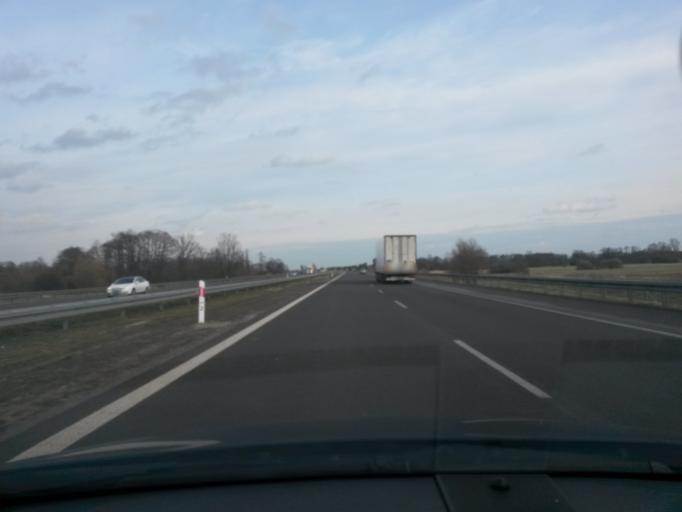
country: PL
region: Greater Poland Voivodeship
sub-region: Powiat turecki
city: Brudzew
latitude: 52.1262
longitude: 18.6726
